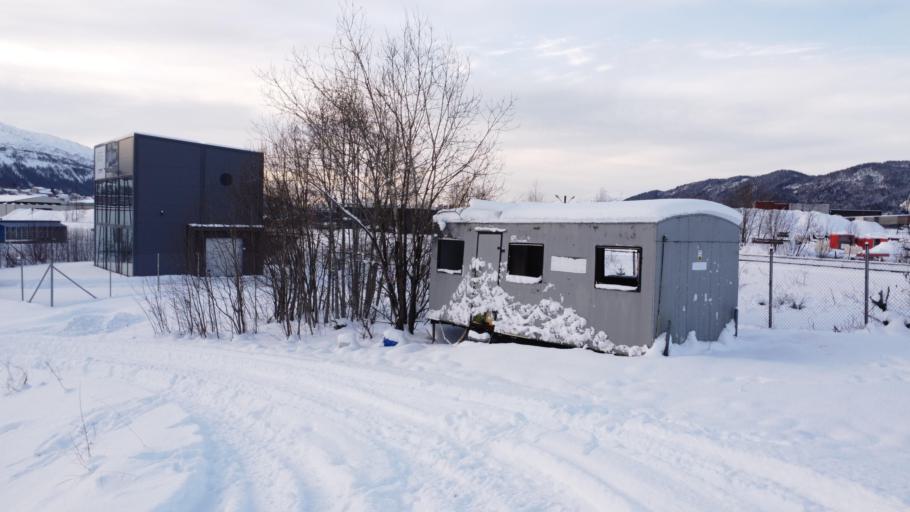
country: NO
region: Nordland
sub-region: Rana
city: Mo i Rana
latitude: 66.3250
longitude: 14.1529
